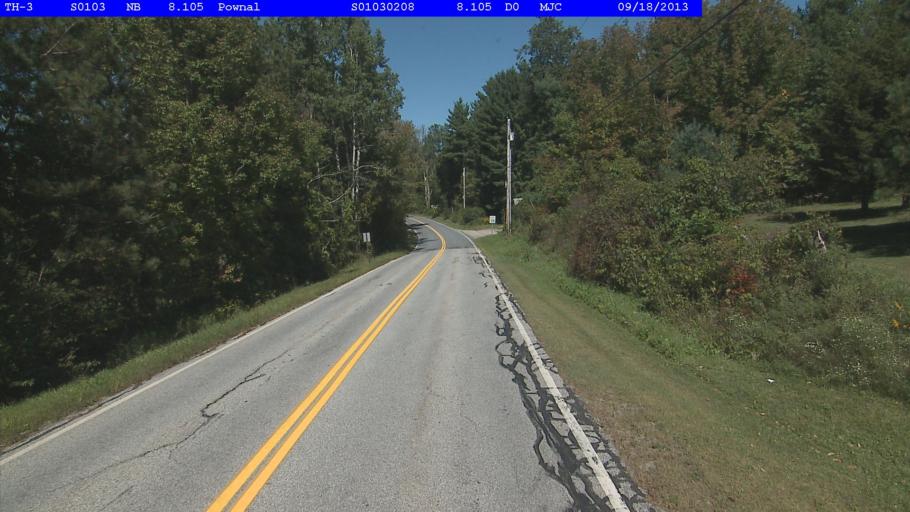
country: US
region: Vermont
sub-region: Bennington County
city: Bennington
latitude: 42.8364
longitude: -73.1703
